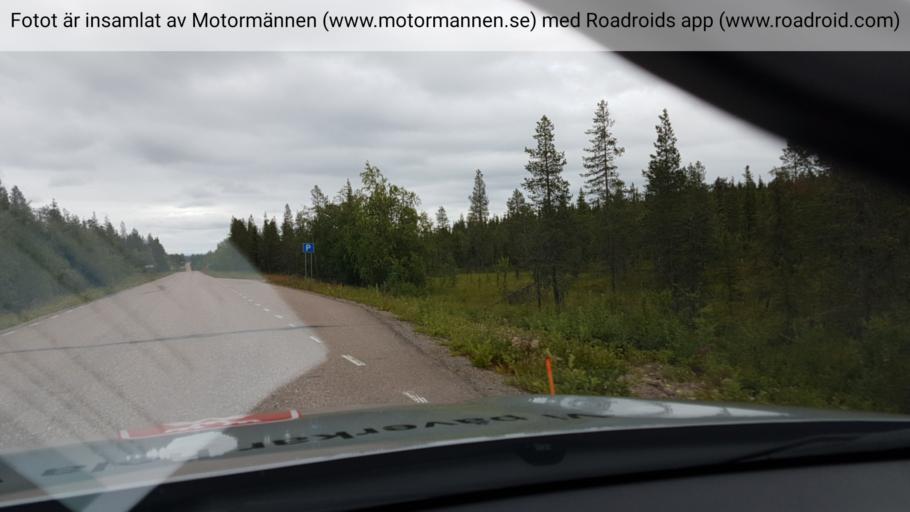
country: SE
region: Norrbotten
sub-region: Overkalix Kommun
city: OEverkalix
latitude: 67.0451
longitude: 22.0676
